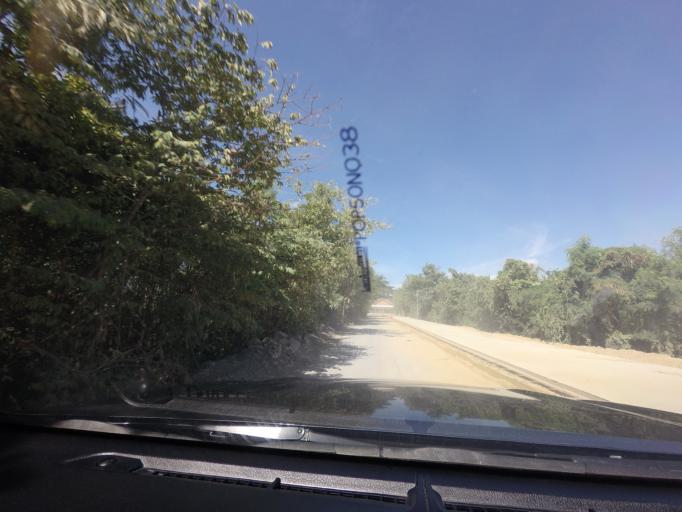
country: TH
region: Suphan Buri
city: Song Phi Nong
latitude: 14.1650
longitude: 100.0072
